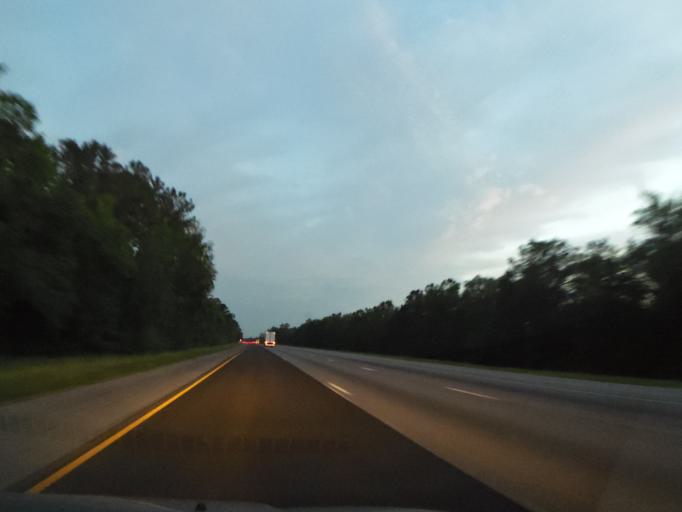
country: US
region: Georgia
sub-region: Liberty County
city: Midway
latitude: 31.7263
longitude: -81.3890
